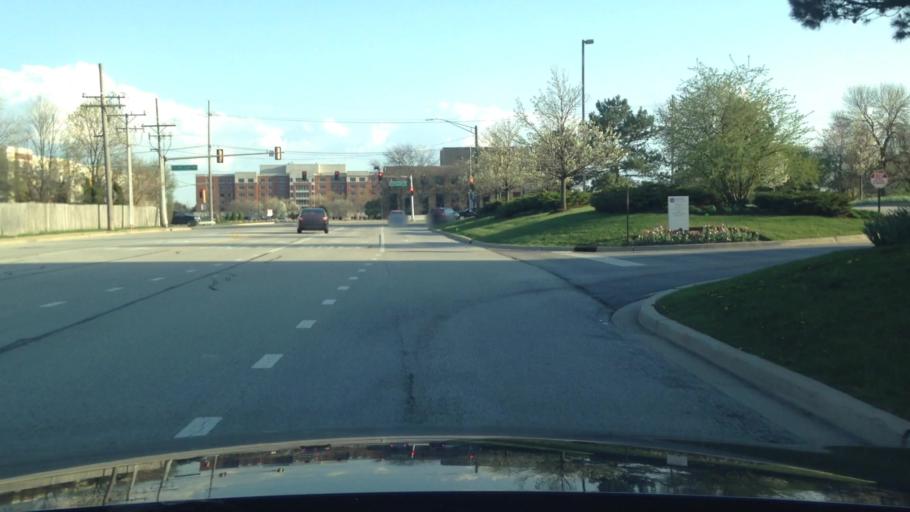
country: US
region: Illinois
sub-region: Lake County
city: Deerfield
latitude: 42.1540
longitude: -87.8675
